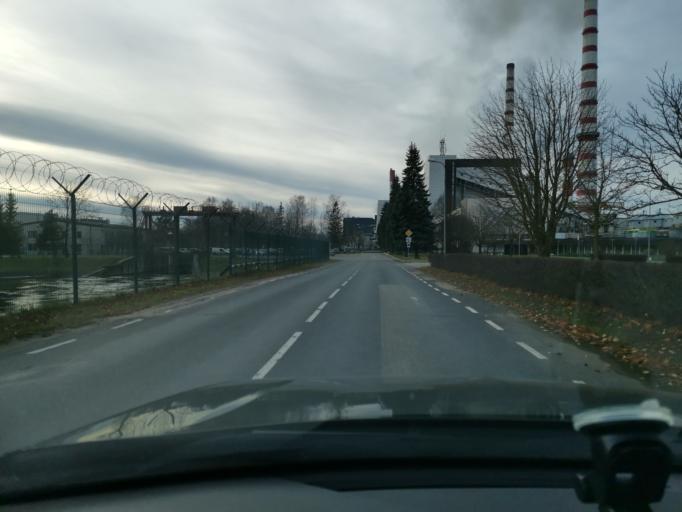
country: EE
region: Ida-Virumaa
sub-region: Sillamaee linn
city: Sillamae
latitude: 59.2743
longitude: 27.9126
